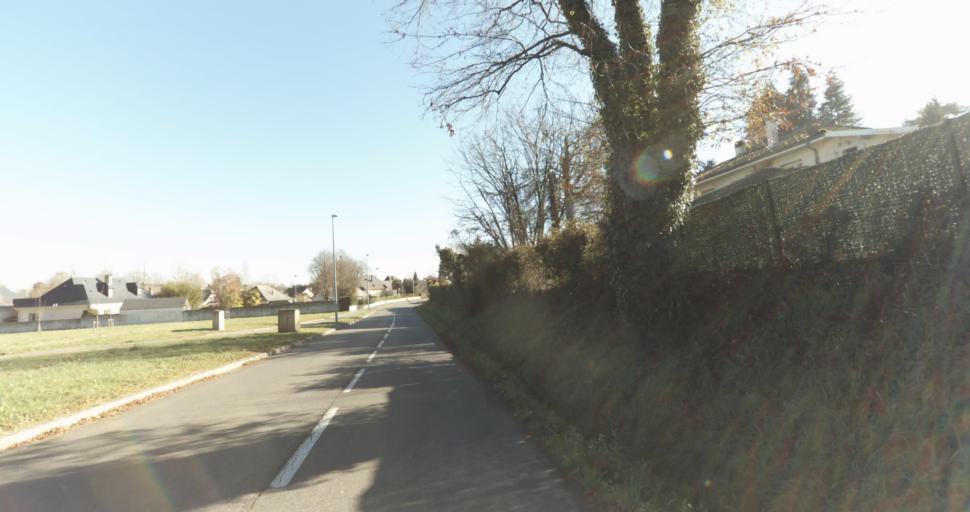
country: FR
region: Aquitaine
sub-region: Departement des Pyrenees-Atlantiques
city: Morlaas
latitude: 43.3440
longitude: -0.2704
